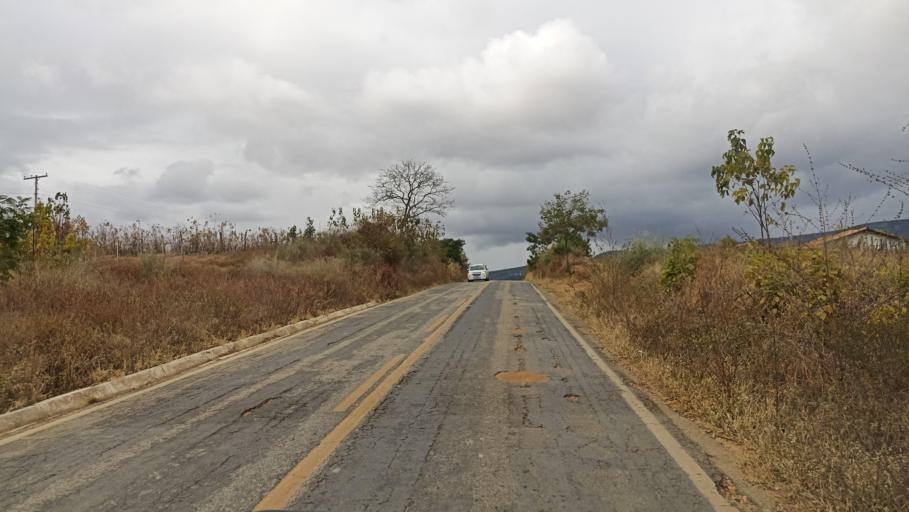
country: BR
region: Minas Gerais
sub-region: Itinga
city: Itinga
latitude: -16.6266
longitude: -41.7849
